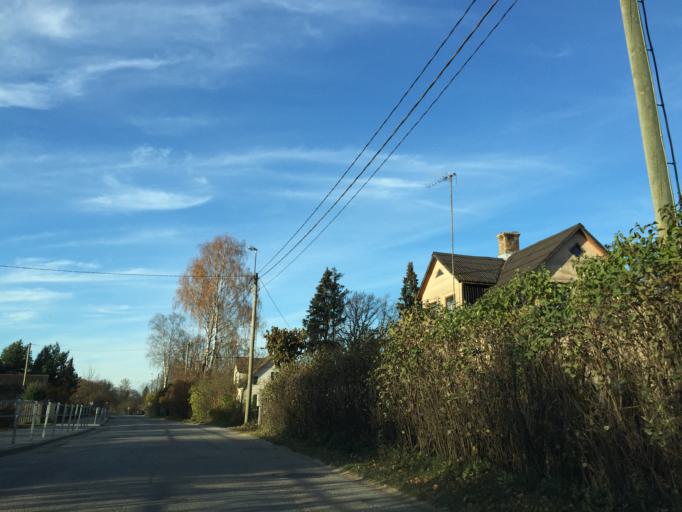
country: LV
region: Skriveri
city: Skriveri
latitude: 56.6384
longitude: 25.1171
